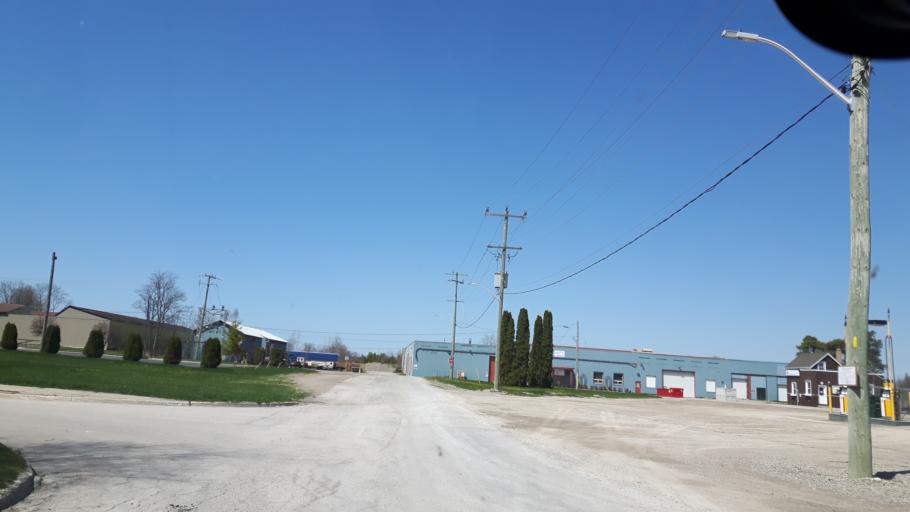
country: CA
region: Ontario
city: Goderich
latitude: 43.7469
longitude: -81.7023
